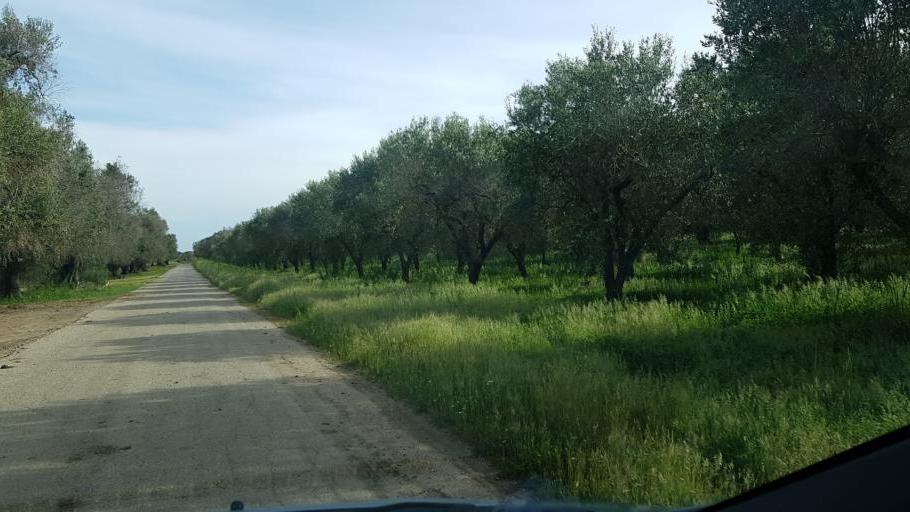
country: IT
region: Apulia
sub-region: Provincia di Brindisi
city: Tuturano
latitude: 40.5297
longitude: 17.9666
